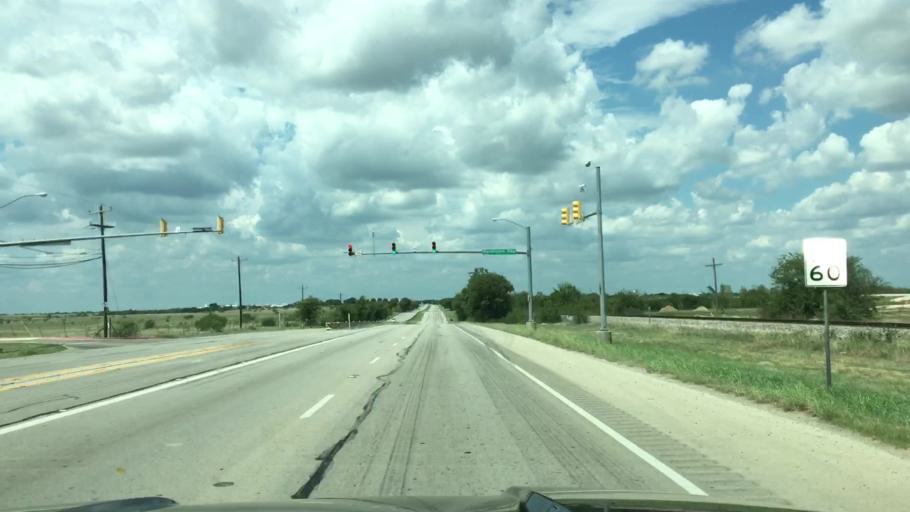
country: US
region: Texas
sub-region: Tarrant County
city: Eagle Mountain
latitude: 32.9081
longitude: -97.4039
